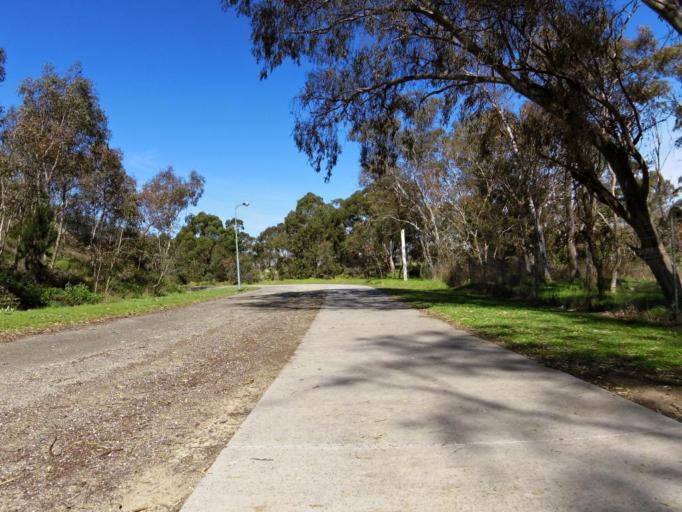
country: AU
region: Victoria
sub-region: Greater Dandenong
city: Dandenong
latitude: -37.9794
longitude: 145.1921
